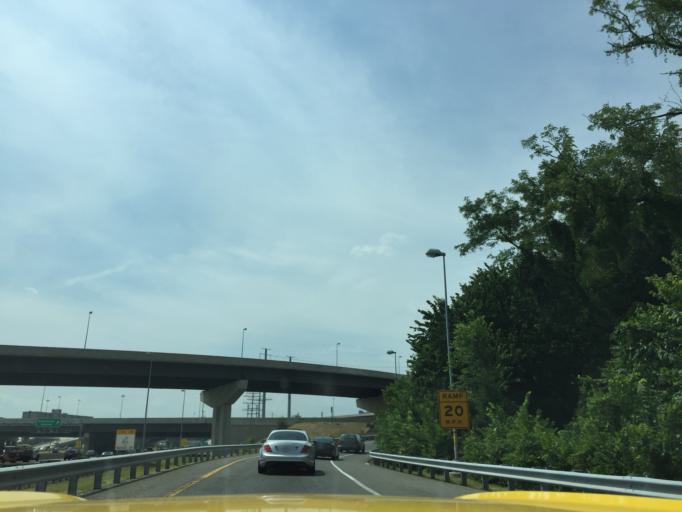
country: US
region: Virginia
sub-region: City of Alexandria
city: Alexandria
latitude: 38.7944
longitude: -77.0517
